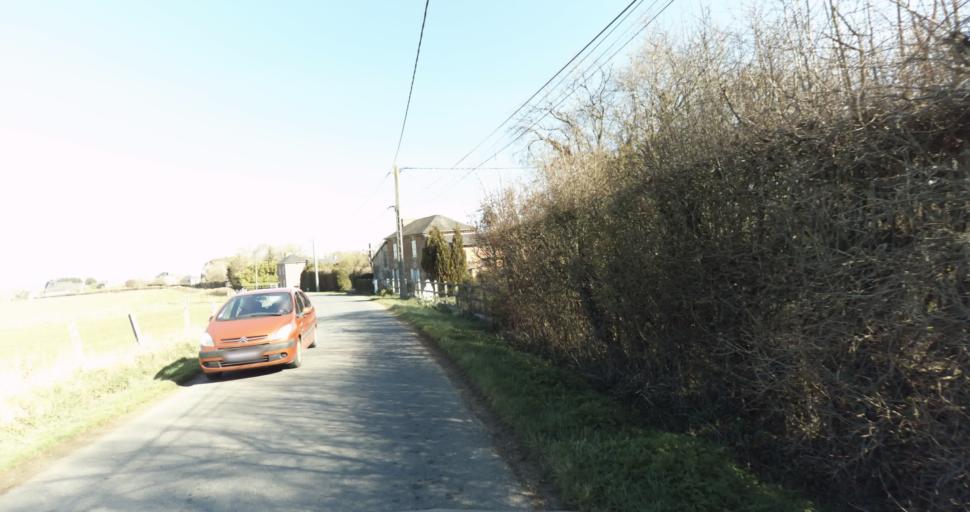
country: FR
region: Lower Normandy
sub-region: Departement de l'Orne
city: Trun
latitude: 48.9132
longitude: 0.0332
